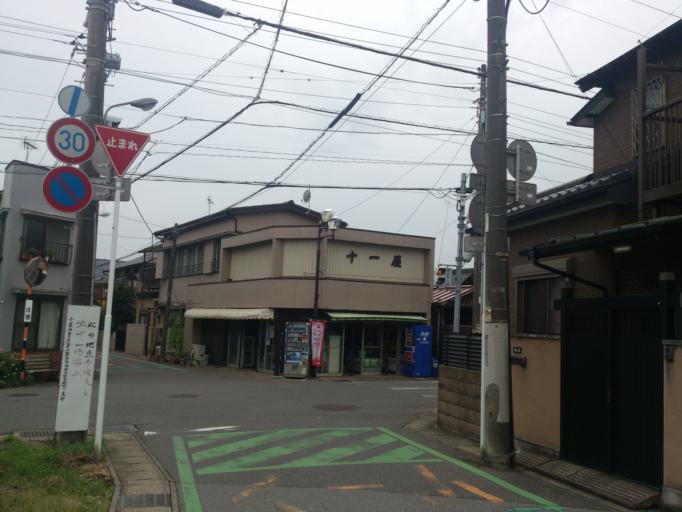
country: JP
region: Chiba
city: Chiba
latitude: 35.6495
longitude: 140.0656
